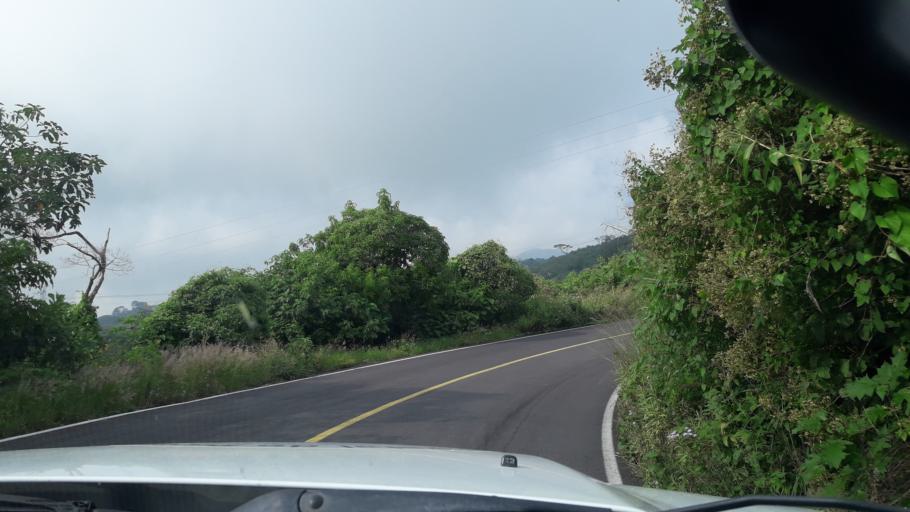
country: MX
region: Colima
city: Queseria
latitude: 19.4090
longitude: -103.6360
